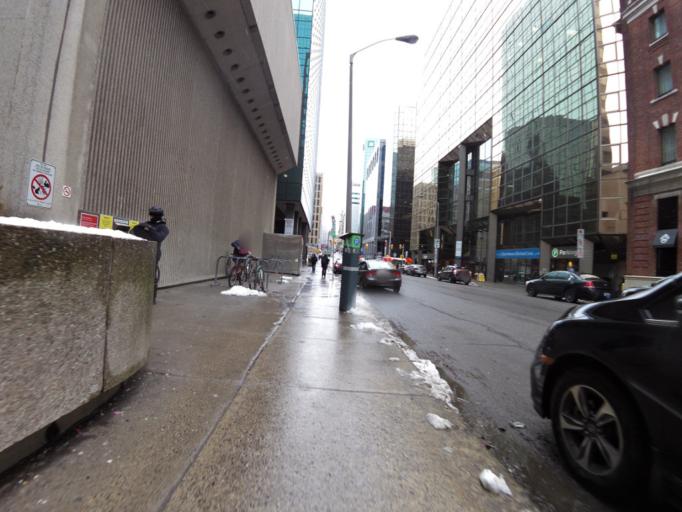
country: CA
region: Ontario
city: Ottawa
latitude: 45.4203
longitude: -75.6954
